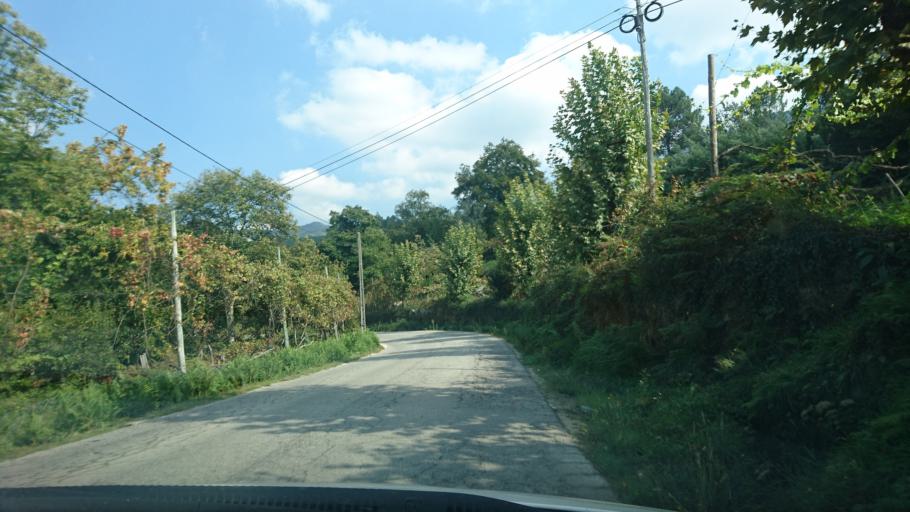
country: PT
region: Vila Real
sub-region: Mondim de Basto
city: Mondim de Basto
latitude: 41.4283
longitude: -7.9331
